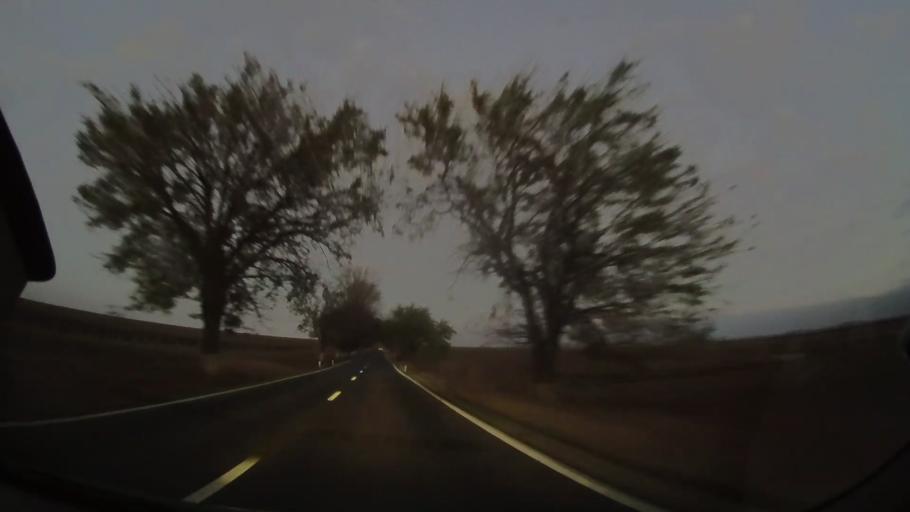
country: RO
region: Tulcea
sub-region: Comuna Frecatei
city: Frecatei
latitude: 45.0806
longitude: 28.6894
